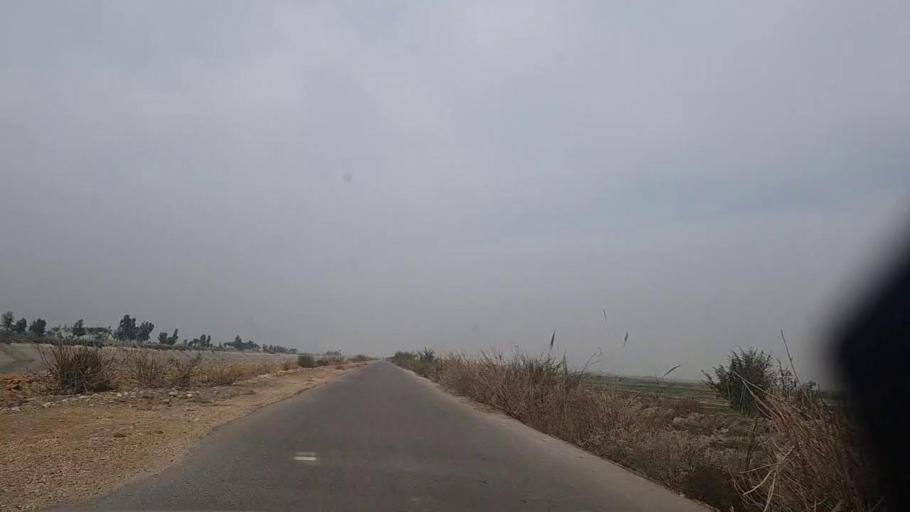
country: PK
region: Sindh
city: Sakrand
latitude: 26.2599
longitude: 68.2435
